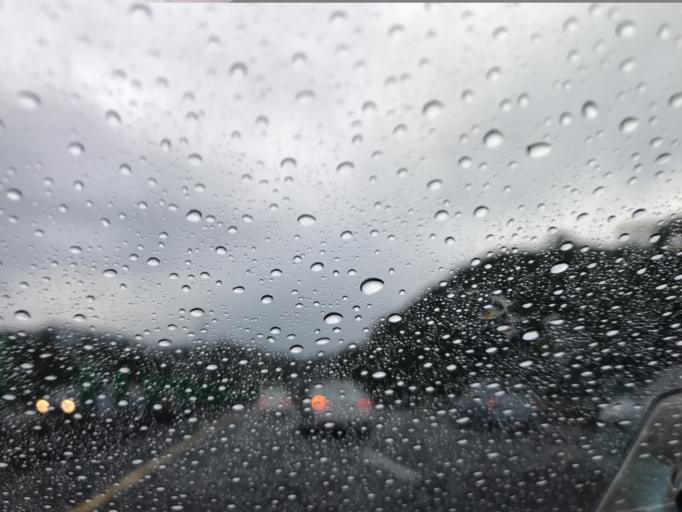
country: TW
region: Taiwan
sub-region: Hsinchu
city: Zhubei
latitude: 24.7851
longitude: 121.1222
